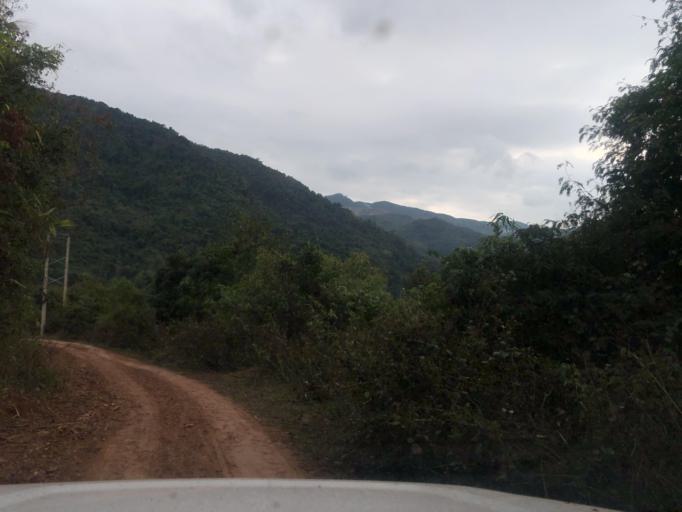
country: LA
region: Phongsali
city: Khoa
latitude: 21.2917
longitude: 102.5844
